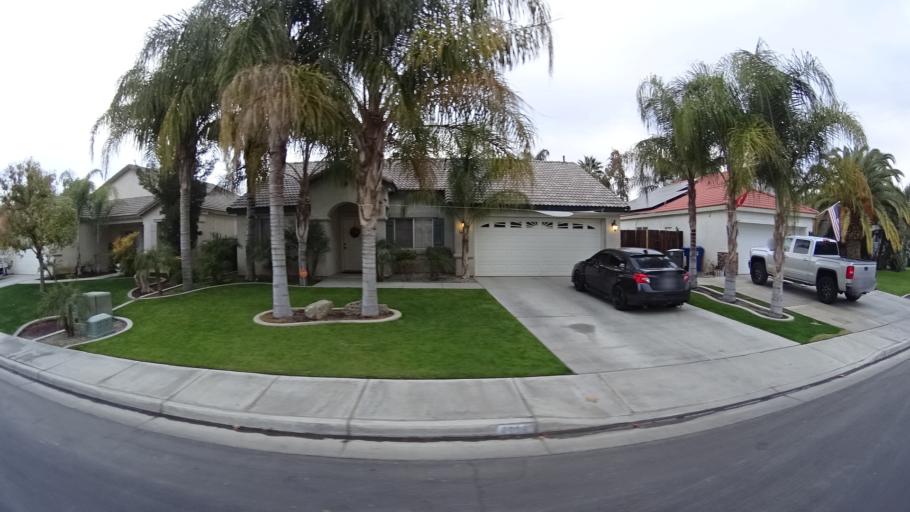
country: US
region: California
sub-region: Kern County
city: Greenfield
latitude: 35.2983
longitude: -119.0793
